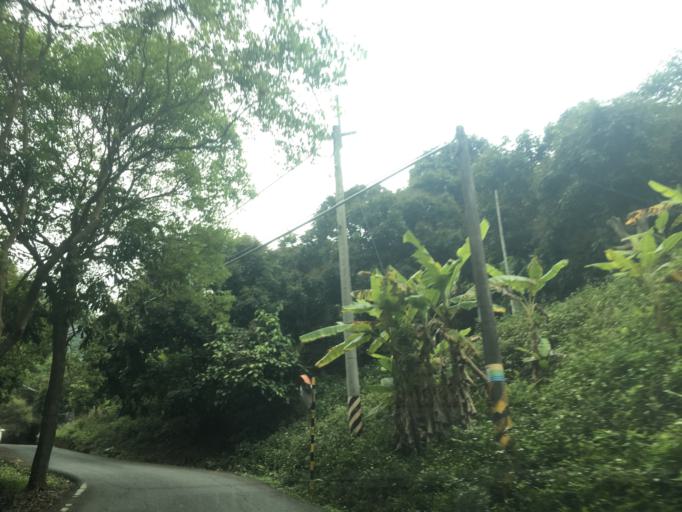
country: TW
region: Taiwan
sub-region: Taichung City
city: Taichung
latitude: 24.0588
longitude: 120.7704
